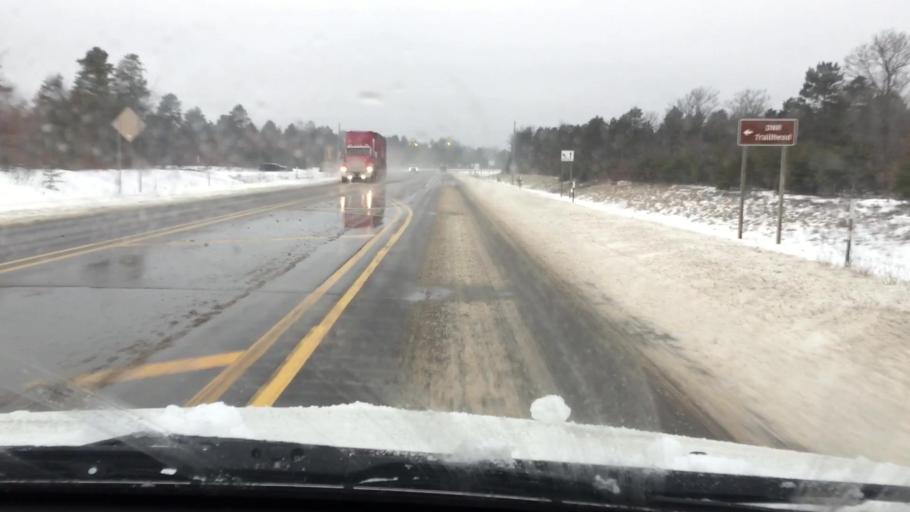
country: US
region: Michigan
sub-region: Wexford County
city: Manton
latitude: 44.4673
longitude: -85.3995
